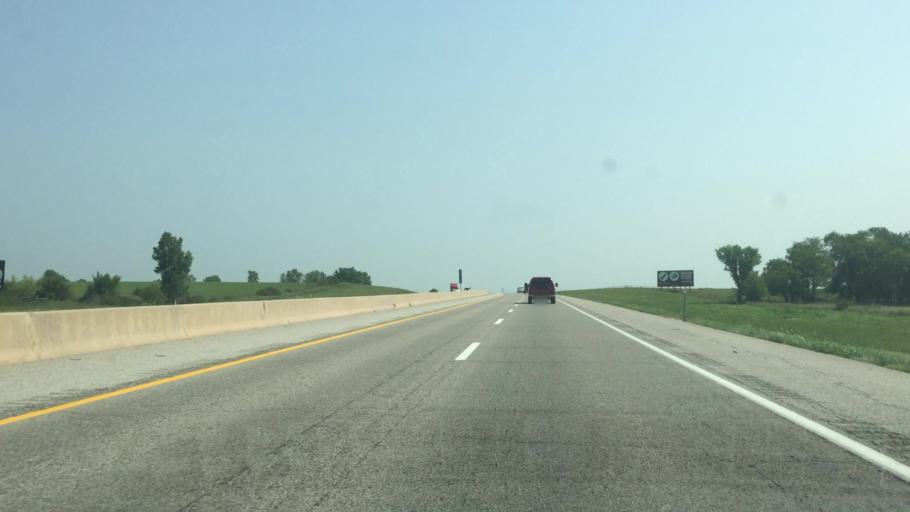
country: US
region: Kansas
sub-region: Lyon County
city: Emporia
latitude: 38.3390
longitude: -96.2972
